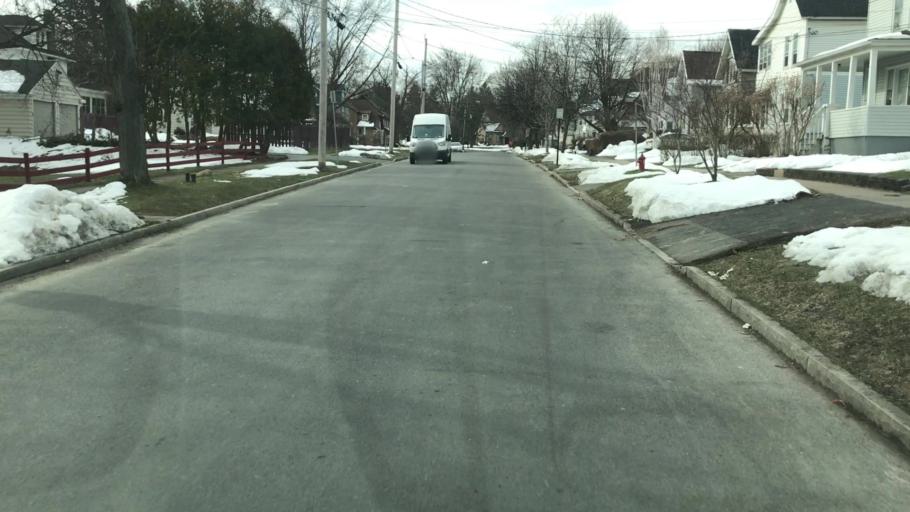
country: US
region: New York
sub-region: Onondaga County
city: Lyncourt
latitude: 43.0653
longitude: -76.1340
